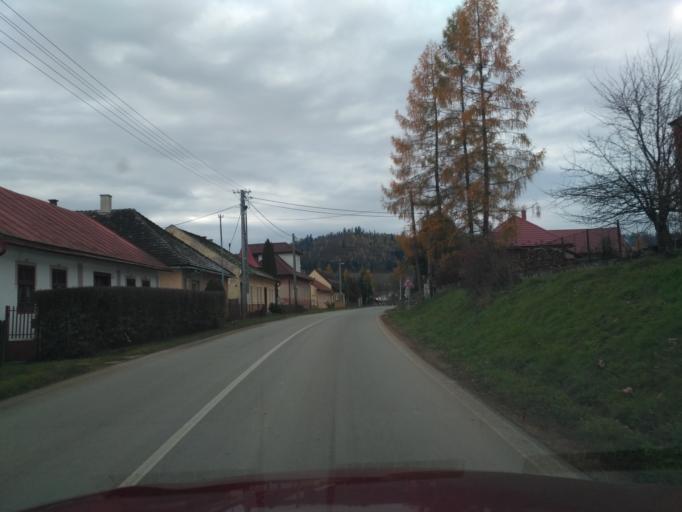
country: SK
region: Kosicky
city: Spisska Nova Ves
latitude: 48.8130
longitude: 20.7024
